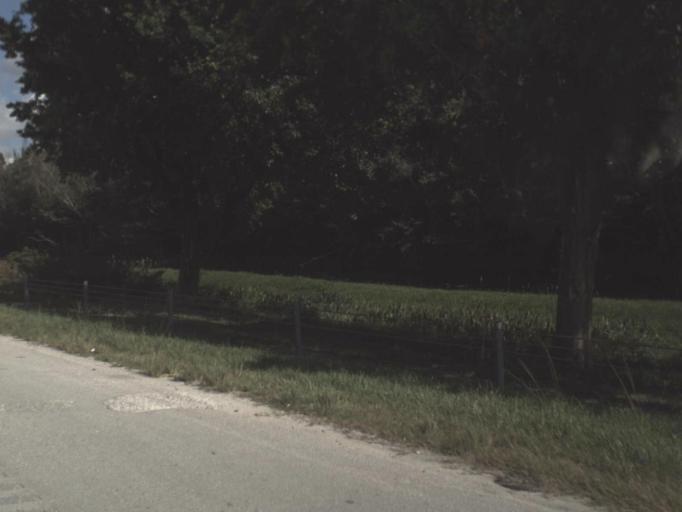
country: US
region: Florida
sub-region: Miami-Dade County
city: Palm Springs North
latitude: 25.9141
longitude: -80.3803
